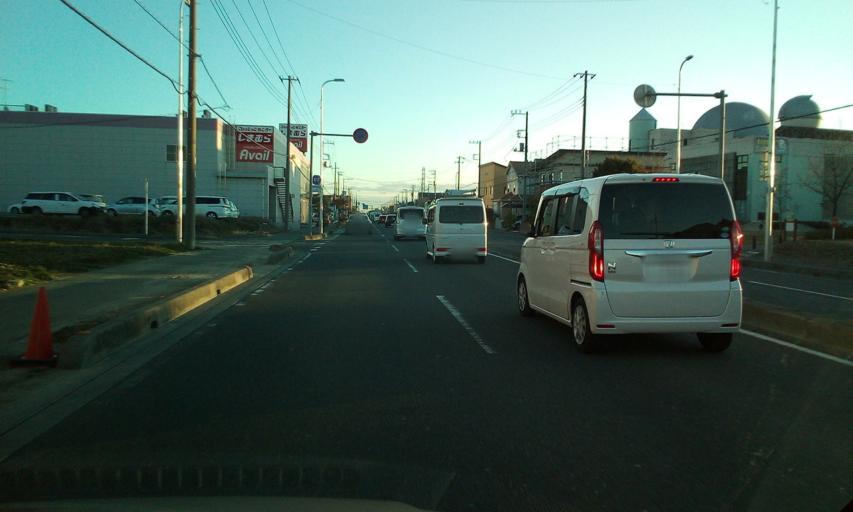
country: JP
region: Saitama
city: Yoshikawa
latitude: 35.8696
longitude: 139.8480
